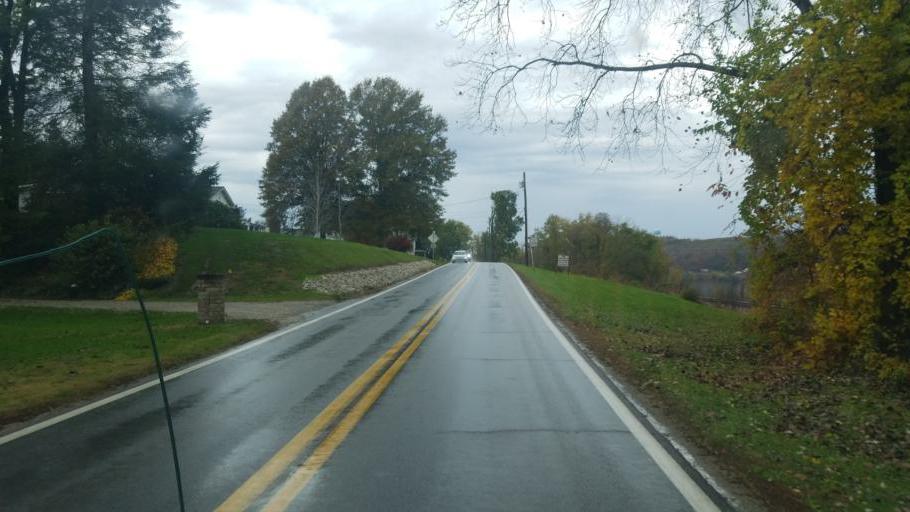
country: US
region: West Virginia
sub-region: Wood County
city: Williamstown
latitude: 39.4025
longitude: -81.4608
